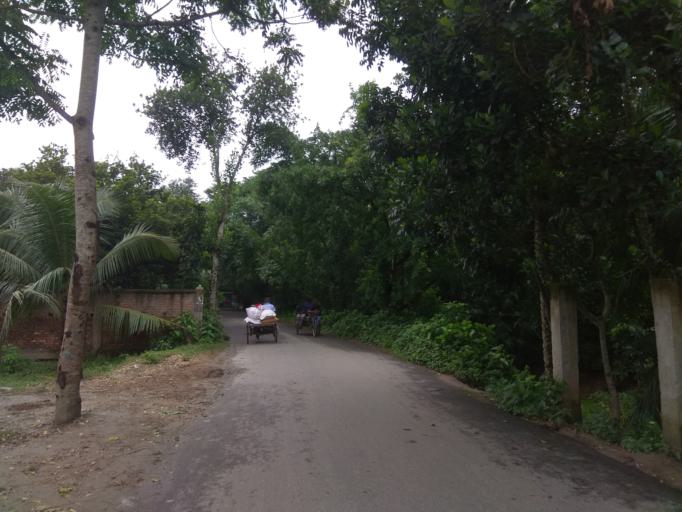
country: BD
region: Dhaka
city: Dohar
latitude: 23.4312
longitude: 90.0721
